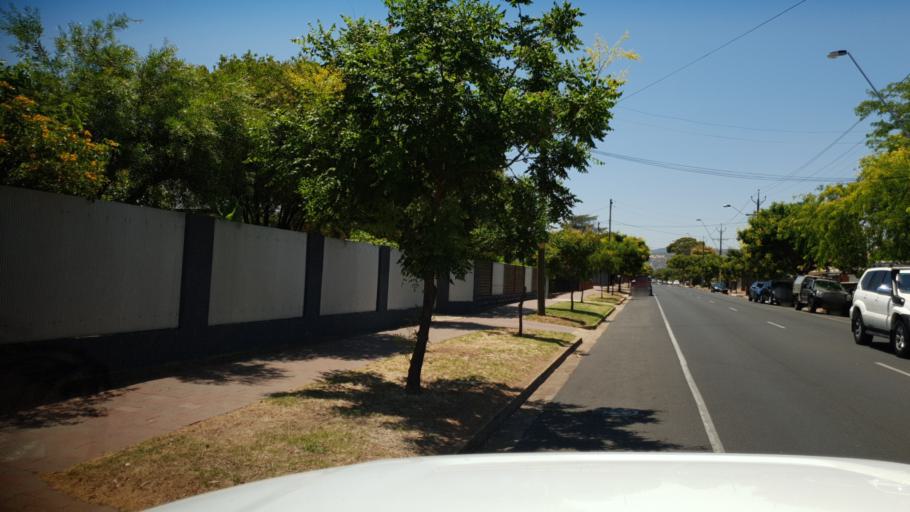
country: AU
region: South Australia
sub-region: Mitcham
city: Clarence Gardens
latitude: -34.9776
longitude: 138.5839
